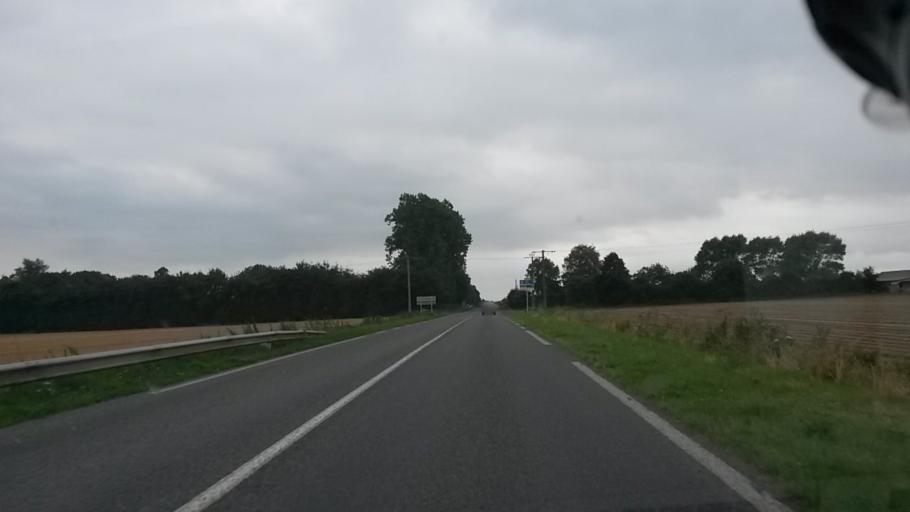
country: FR
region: Haute-Normandie
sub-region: Departement de la Seine-Maritime
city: Aumale
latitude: 49.7672
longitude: 1.7989
